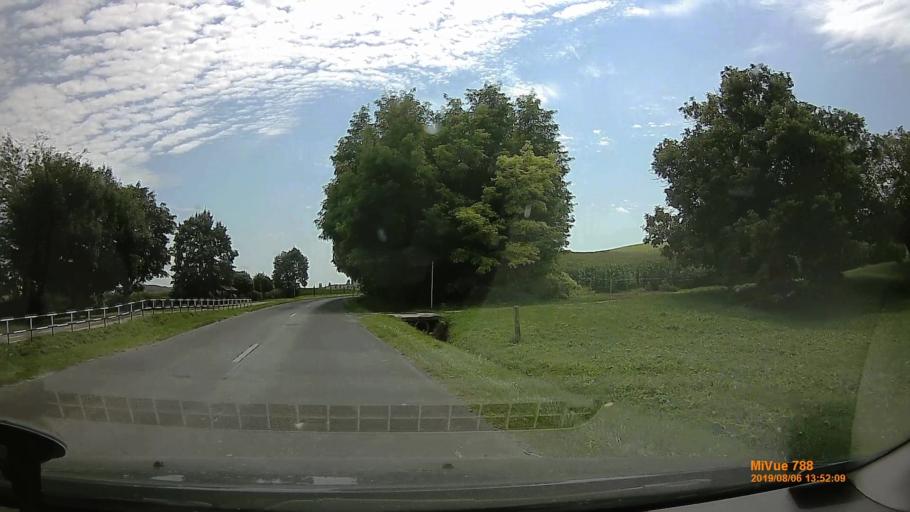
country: HU
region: Zala
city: Zalakomar
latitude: 46.5768
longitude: 17.1234
